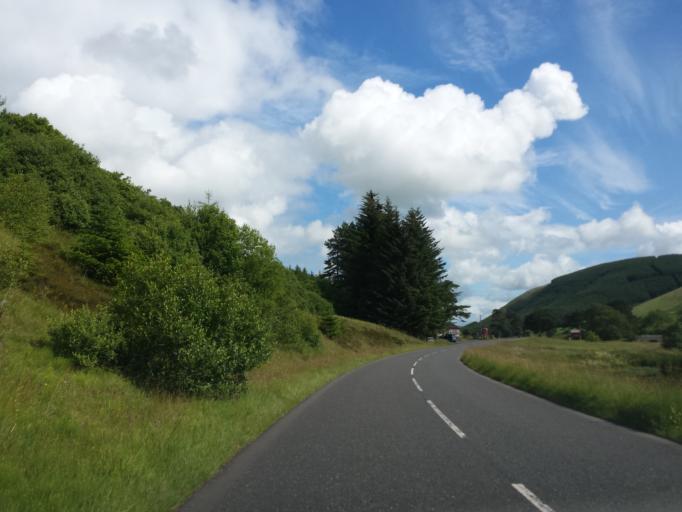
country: GB
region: Scotland
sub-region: The Scottish Borders
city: Peebles
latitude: 55.4703
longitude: -3.2083
